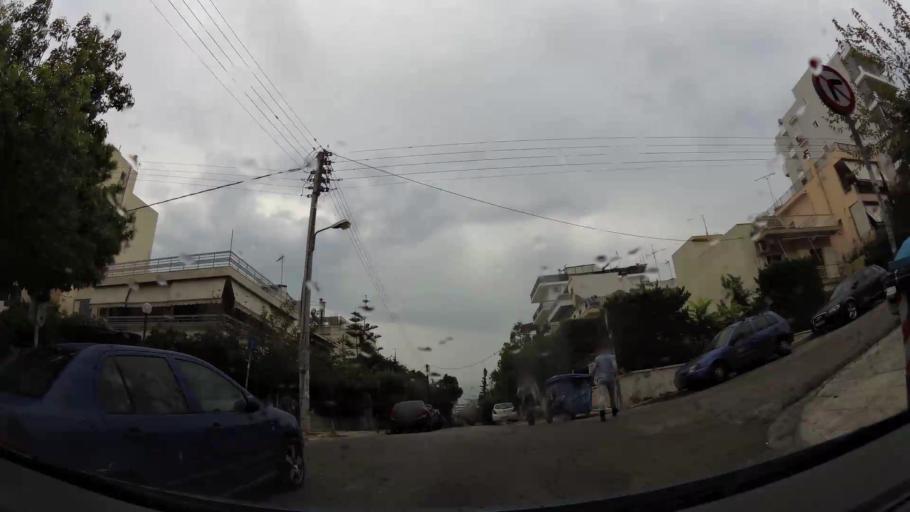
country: GR
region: Attica
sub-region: Nomarchia Athinas
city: Palaio Faliro
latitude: 37.9309
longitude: 23.6983
